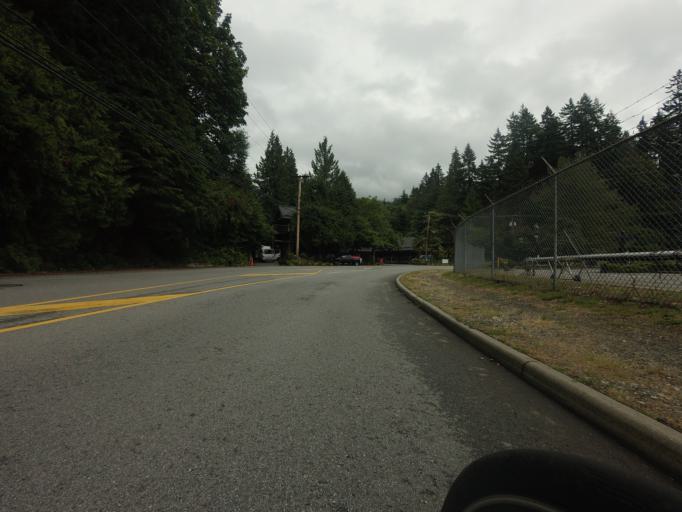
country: CA
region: British Columbia
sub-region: Greater Vancouver Regional District
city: Bowen Island
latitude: 49.3587
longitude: -123.2681
